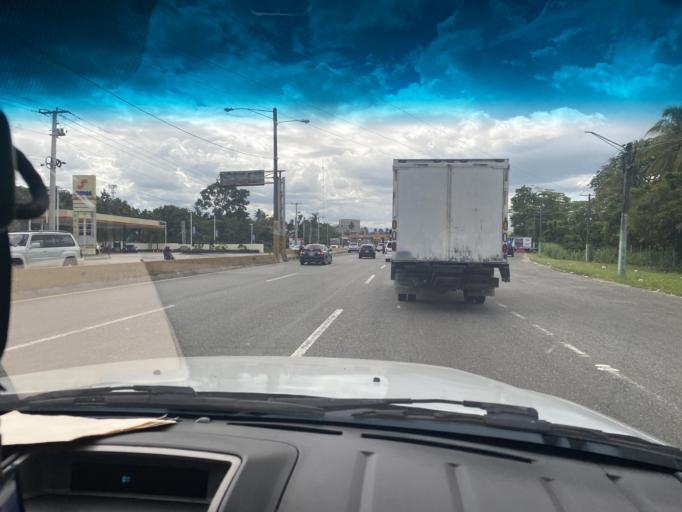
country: DO
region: Santo Domingo
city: Santo Domingo Oeste
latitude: 18.5661
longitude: -70.0827
